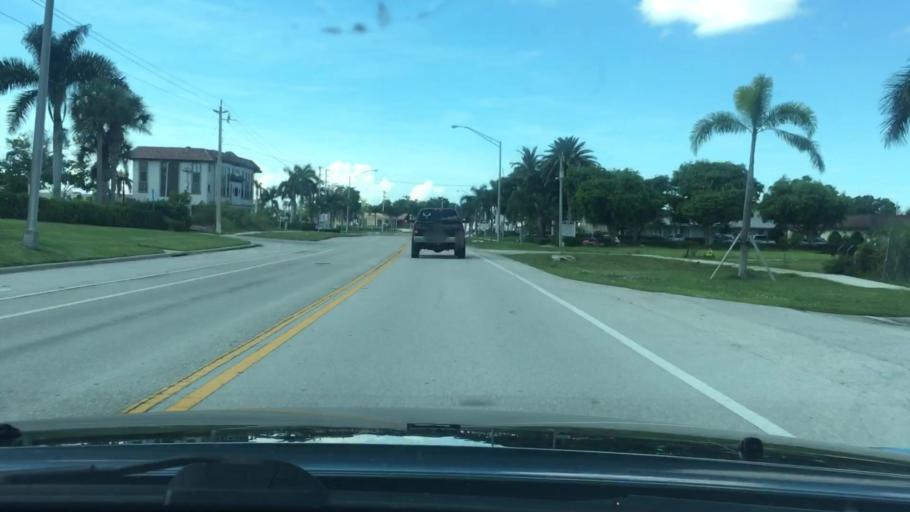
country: US
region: Florida
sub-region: Collier County
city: Marco
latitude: 25.9355
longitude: -81.6965
